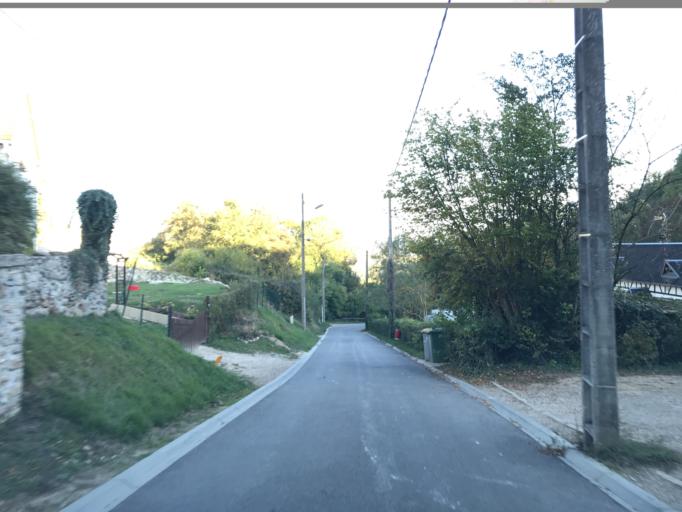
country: FR
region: Haute-Normandie
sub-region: Departement de l'Eure
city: Houlbec-Cocherel
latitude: 49.0734
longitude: 1.2742
